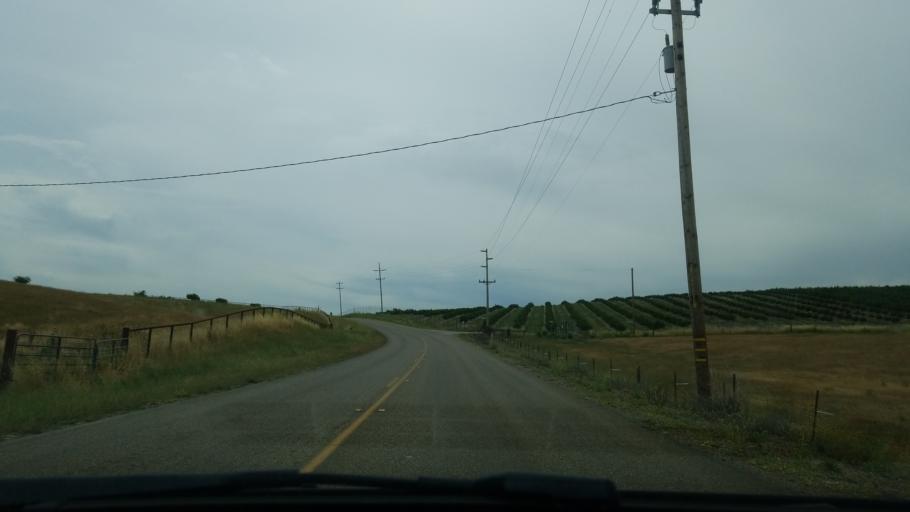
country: US
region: California
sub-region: San Luis Obispo County
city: Pismo Beach
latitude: 35.2098
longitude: -120.5861
